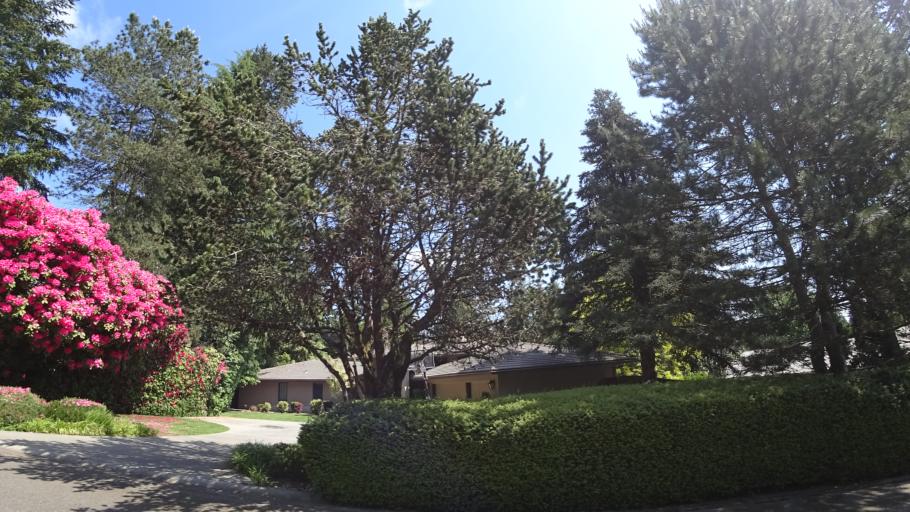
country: US
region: Oregon
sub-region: Clackamas County
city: Lake Oswego
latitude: 45.4312
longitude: -122.7135
